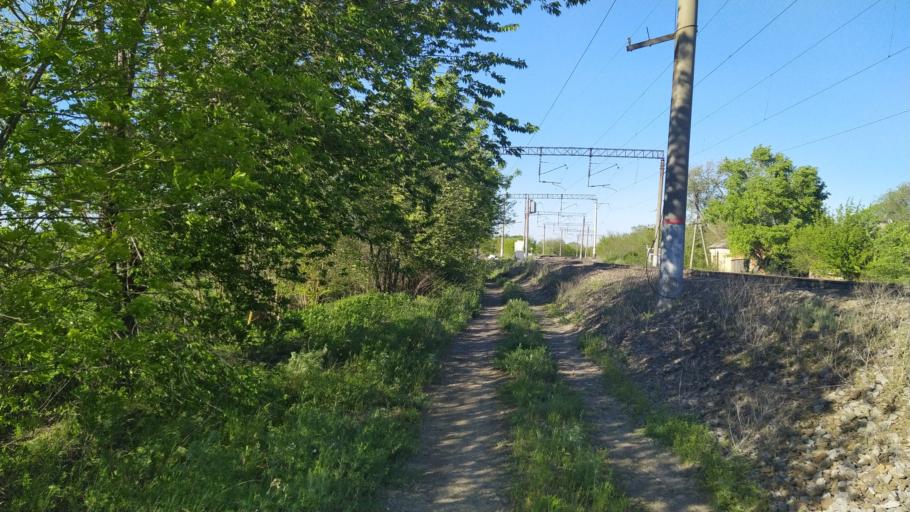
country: RU
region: Rostov
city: Bataysk
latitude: 47.0802
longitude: 39.7207
